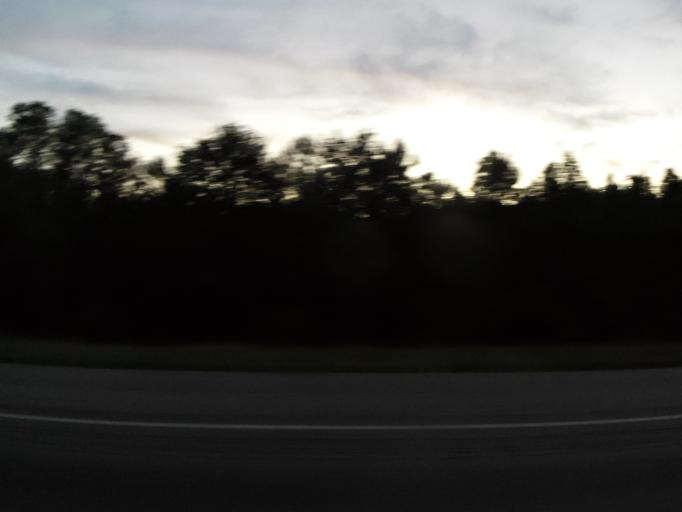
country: US
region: Georgia
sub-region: Liberty County
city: Midway
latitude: 31.7470
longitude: -81.3851
